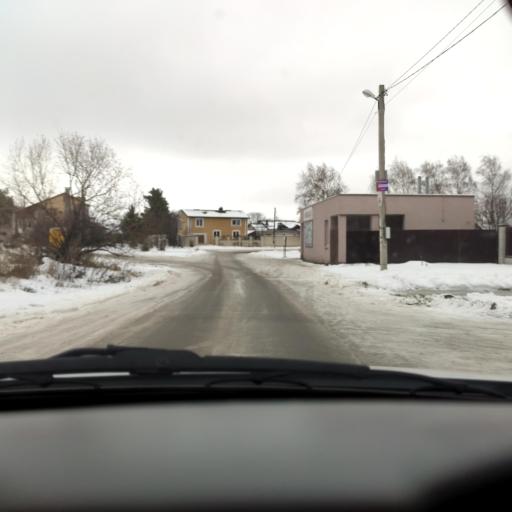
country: RU
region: Voronezj
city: Ramon'
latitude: 51.8877
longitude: 39.2650
